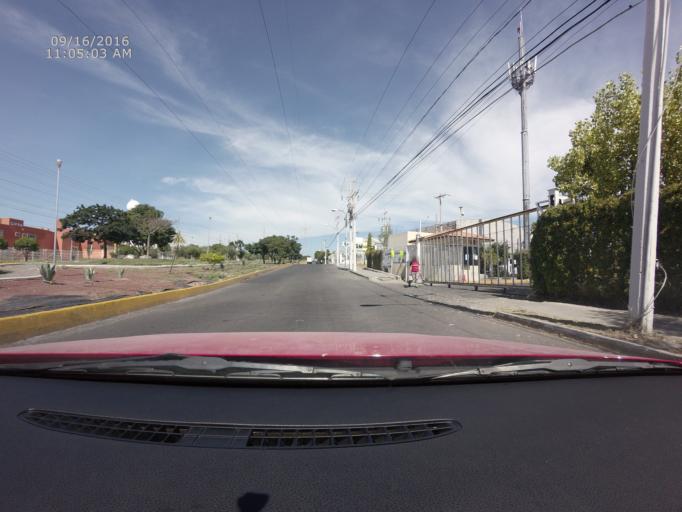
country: MX
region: Queretaro
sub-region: Queretaro
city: Sergio Villasenor
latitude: 20.6263
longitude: -100.4017
